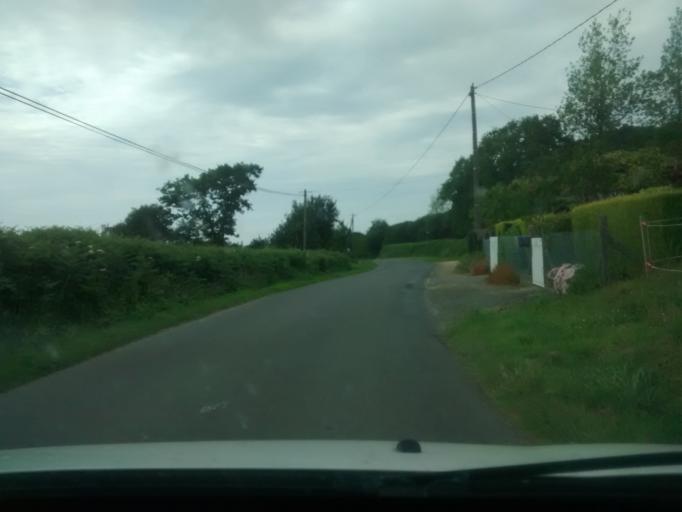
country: FR
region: Brittany
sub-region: Departement des Cotes-d'Armor
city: Trelevern
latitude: 48.8002
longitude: -3.3644
